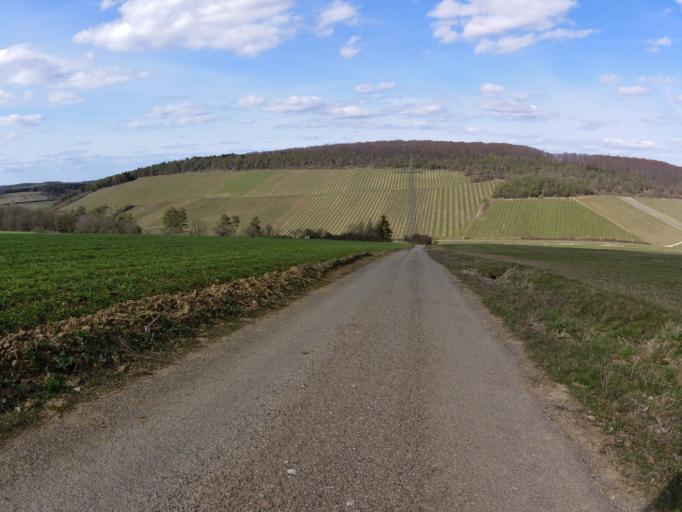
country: DE
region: Bavaria
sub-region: Regierungsbezirk Unterfranken
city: Erlabrunn
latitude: 49.8403
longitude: 9.8173
